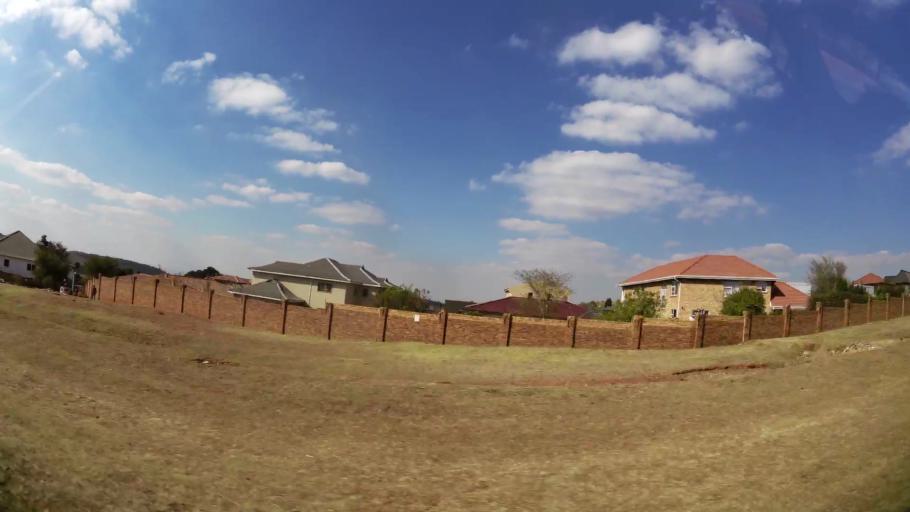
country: ZA
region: Gauteng
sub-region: West Rand District Municipality
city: Krugersdorp
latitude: -26.0551
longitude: 27.7544
